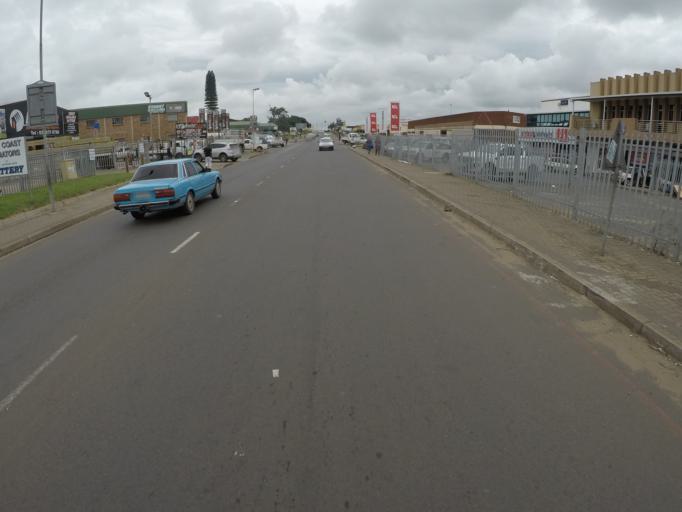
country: ZA
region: KwaZulu-Natal
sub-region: uThungulu District Municipality
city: Empangeni
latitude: -28.7712
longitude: 31.9048
